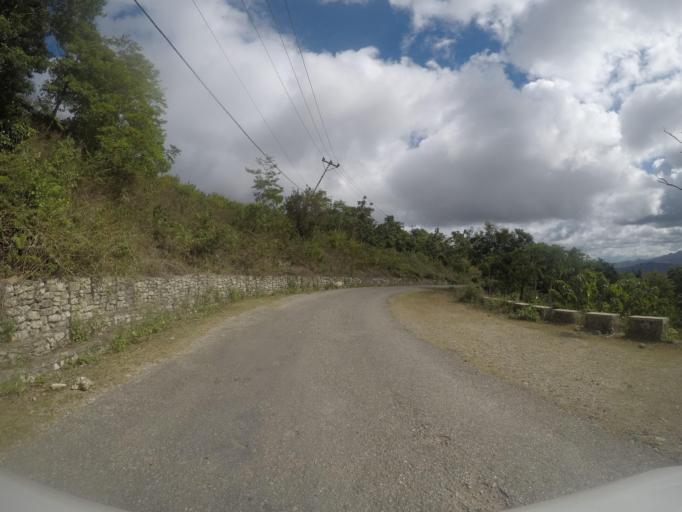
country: TL
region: Lautem
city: Lospalos
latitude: -8.5341
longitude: 126.9140
